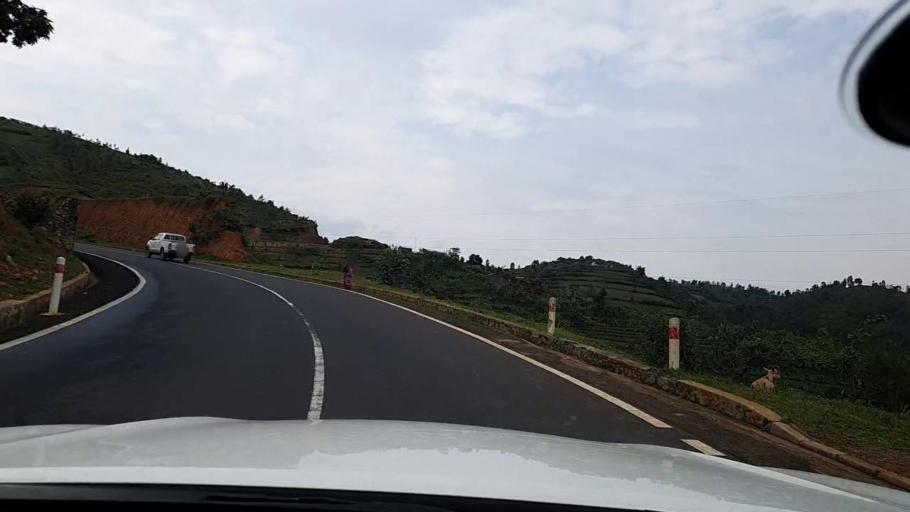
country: RW
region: Western Province
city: Kibuye
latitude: -2.1655
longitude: 29.2924
